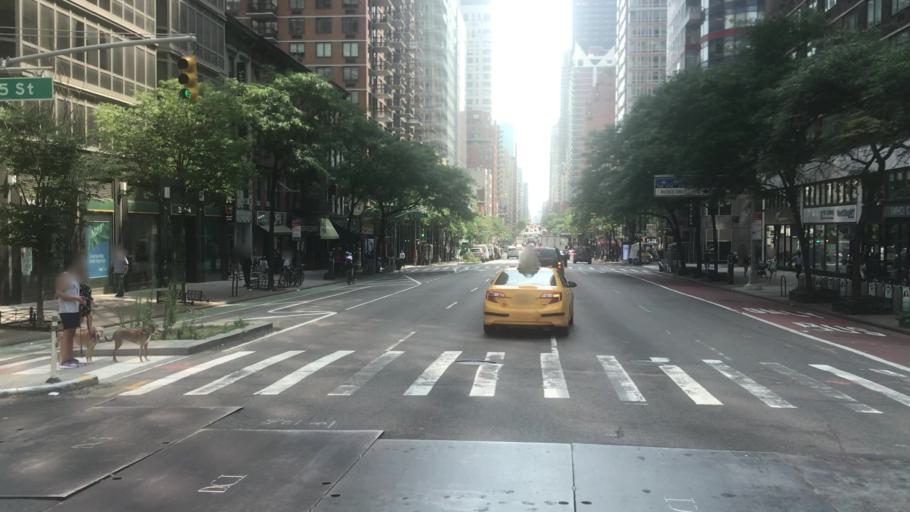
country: US
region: New York
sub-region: Queens County
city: Long Island City
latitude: 40.7580
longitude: -73.9662
